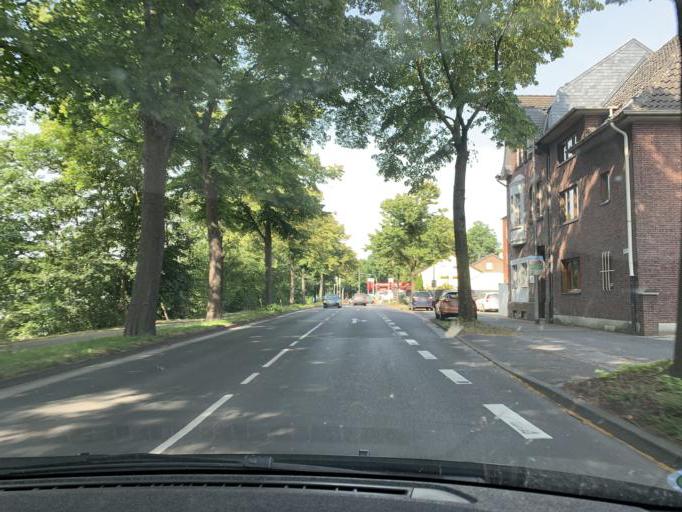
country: DE
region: North Rhine-Westphalia
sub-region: Regierungsbezirk Dusseldorf
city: Viersen
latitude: 51.2570
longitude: 6.3742
